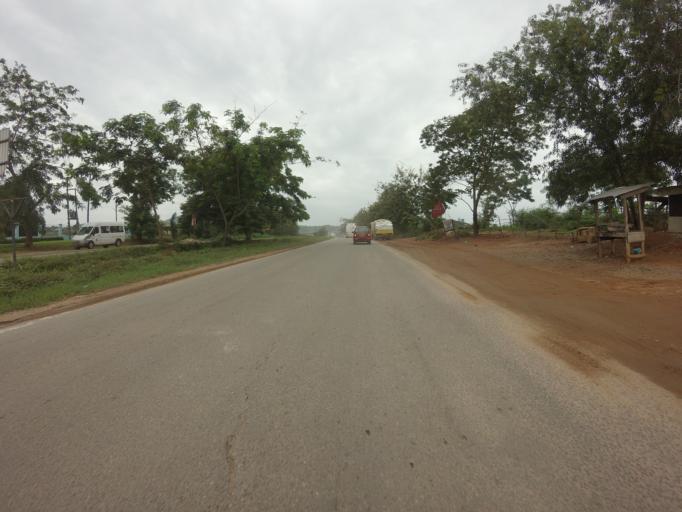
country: GH
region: Eastern
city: Nsawam
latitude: 5.7915
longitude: -0.3396
